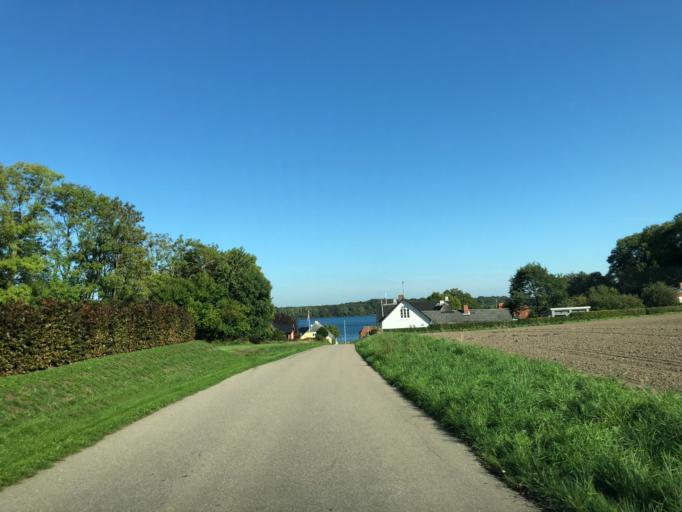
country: DK
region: South Denmark
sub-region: Sonderborg Kommune
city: Dybbol
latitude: 54.9702
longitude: 9.7411
